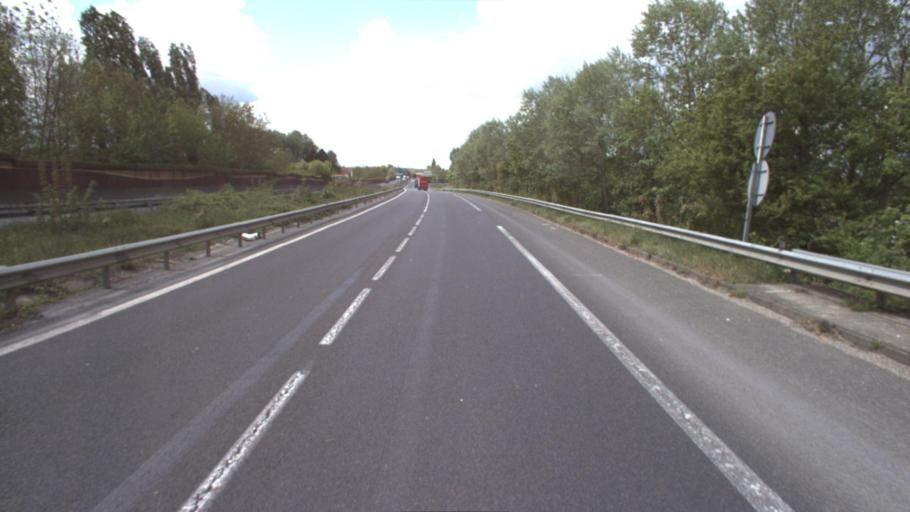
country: FR
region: Ile-de-France
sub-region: Departement de Seine-et-Marne
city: Fontenay-Tresigny
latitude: 48.7126
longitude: 2.8695
